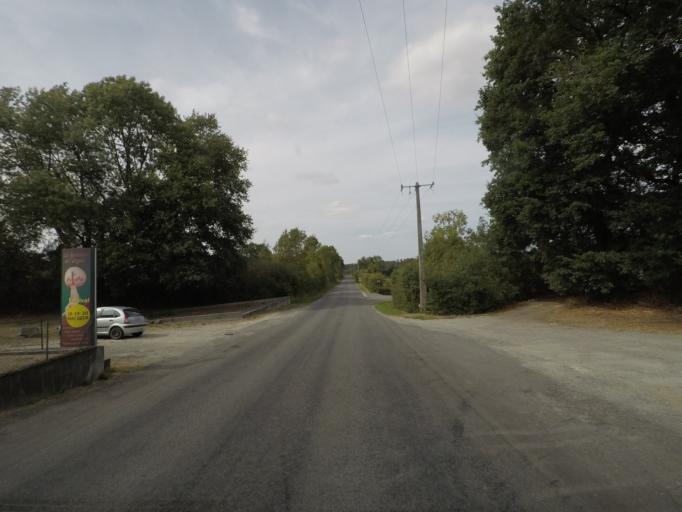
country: FR
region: Poitou-Charentes
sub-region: Departement de la Charente
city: Loubert
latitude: 45.9239
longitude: 0.5523
